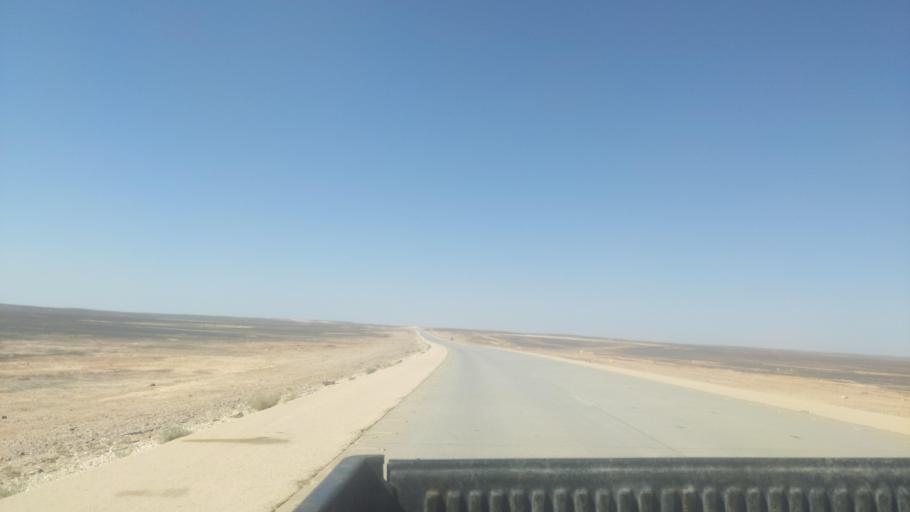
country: JO
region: Amman
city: Al Azraq ash Shamali
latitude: 31.4223
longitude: 36.7256
